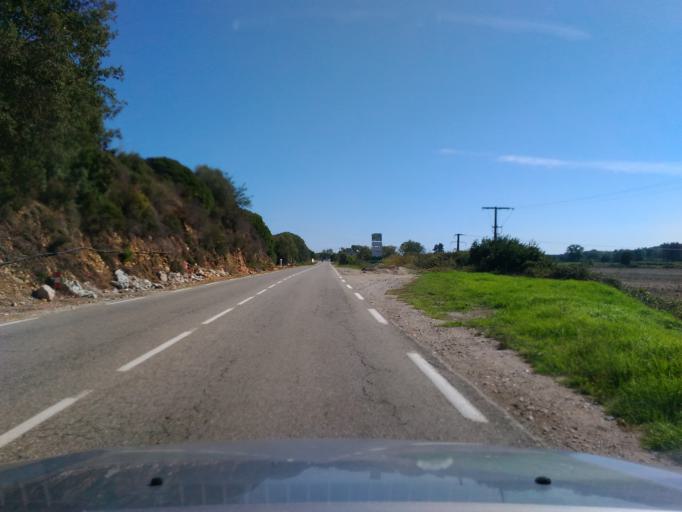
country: FR
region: Corsica
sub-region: Departement de la Haute-Corse
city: Aleria
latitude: 42.1138
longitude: 9.5028
